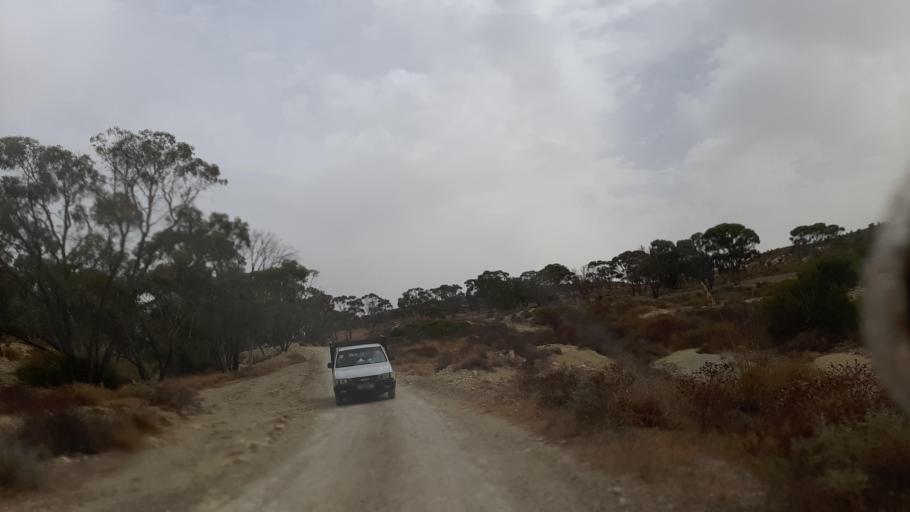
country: TN
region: Tunis
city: La Mohammedia
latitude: 36.5676
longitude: 10.1416
